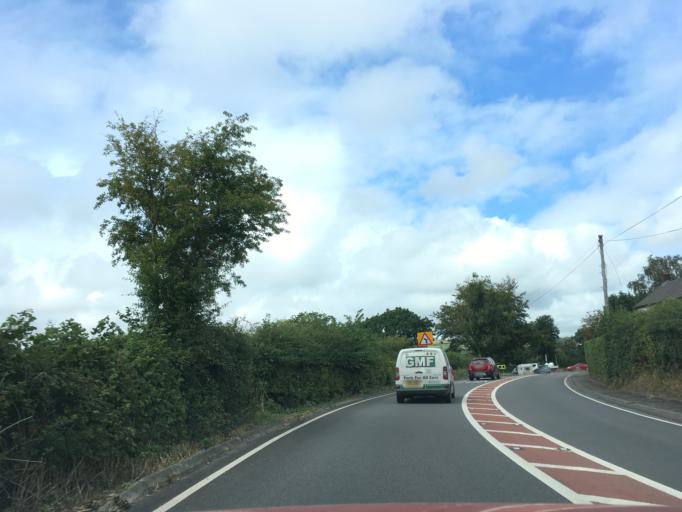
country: GB
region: Wales
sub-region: Carmarthenshire
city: Llanddarog
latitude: 51.8708
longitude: -4.1310
